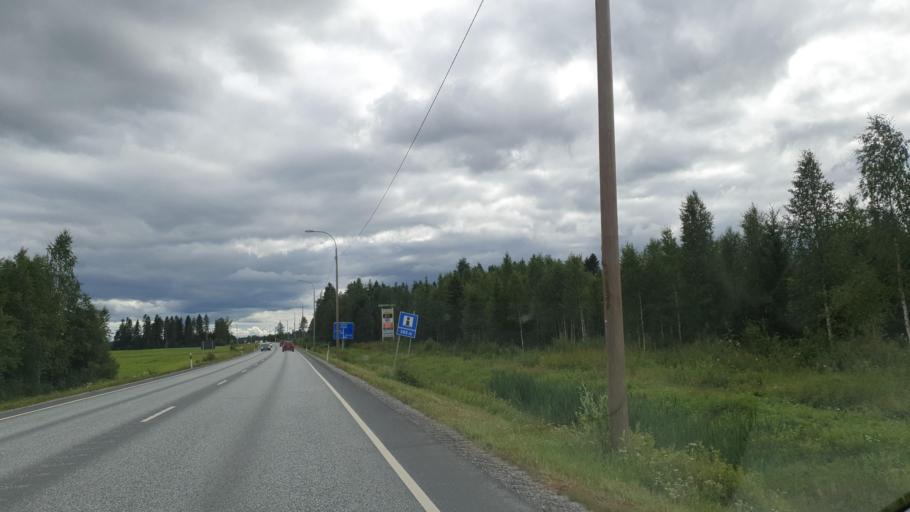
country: FI
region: Northern Savo
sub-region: Ylae-Savo
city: Sonkajaervi
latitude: 63.8737
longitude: 27.4403
